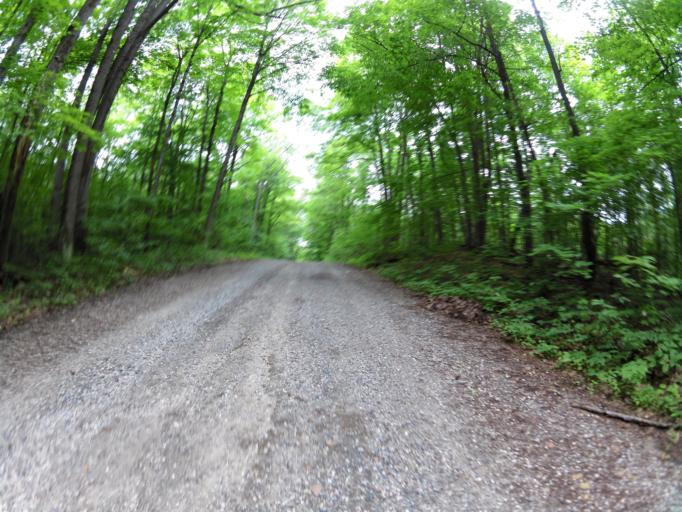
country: CA
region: Ontario
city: Perth
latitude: 45.0280
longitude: -76.5642
